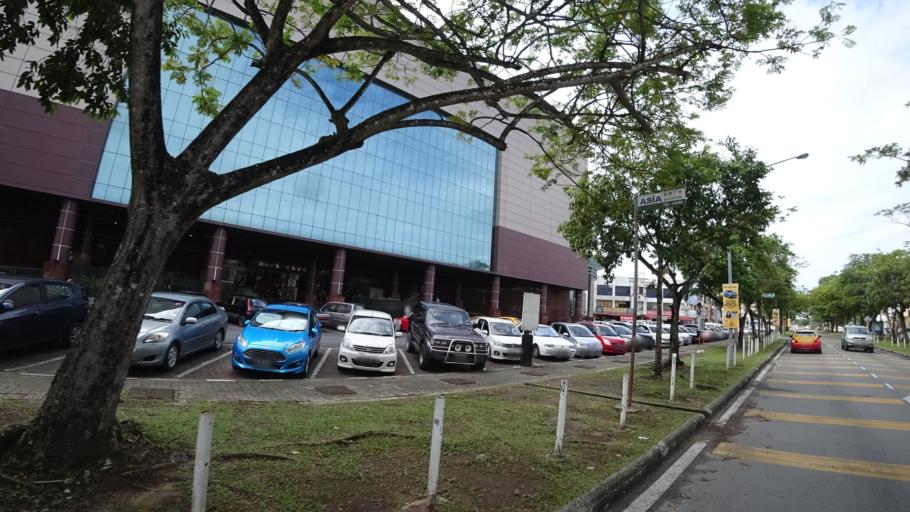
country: MY
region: Sarawak
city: Miri
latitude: 4.4157
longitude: 114.0125
